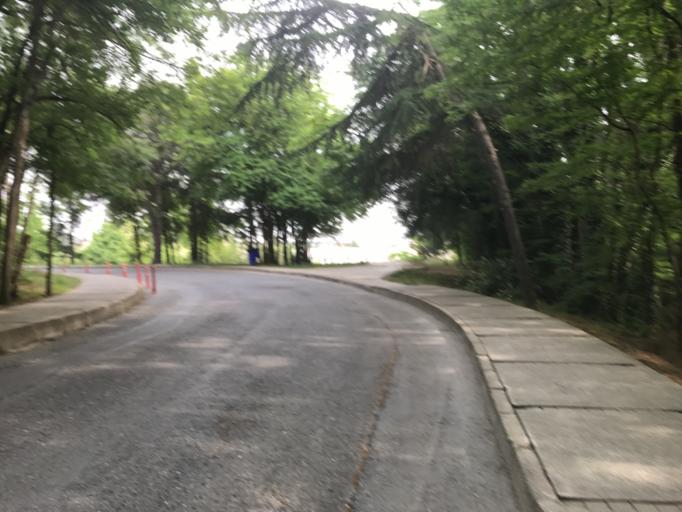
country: TR
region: Istanbul
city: Sisli
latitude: 41.1061
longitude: 29.0189
